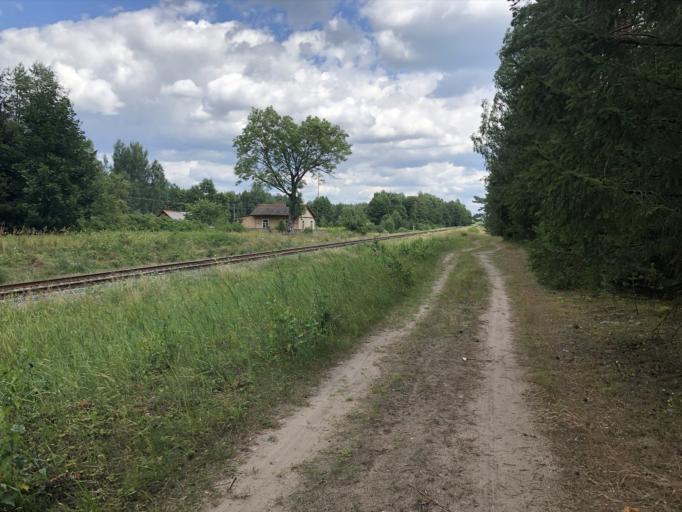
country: LT
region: Alytaus apskritis
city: Druskininkai
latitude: 53.9216
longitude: 24.1872
